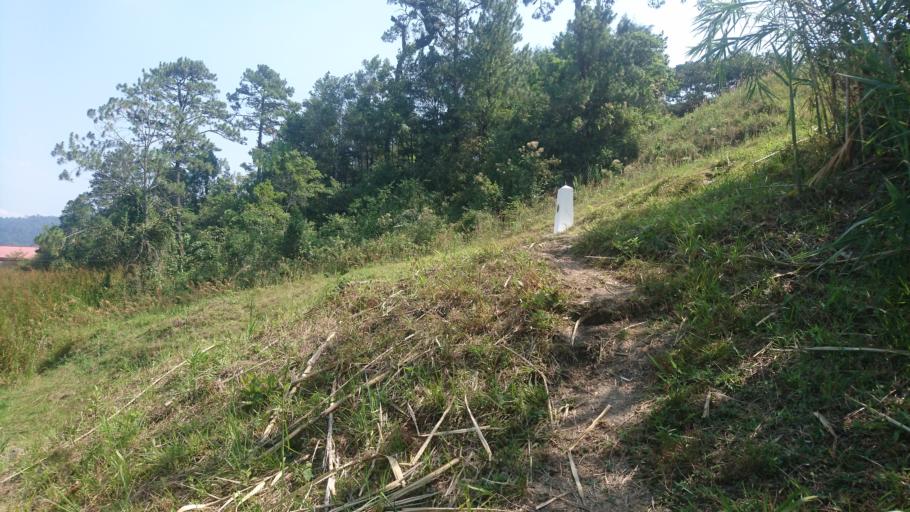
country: GT
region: Huehuetenango
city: Union
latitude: 16.0737
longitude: -91.6805
